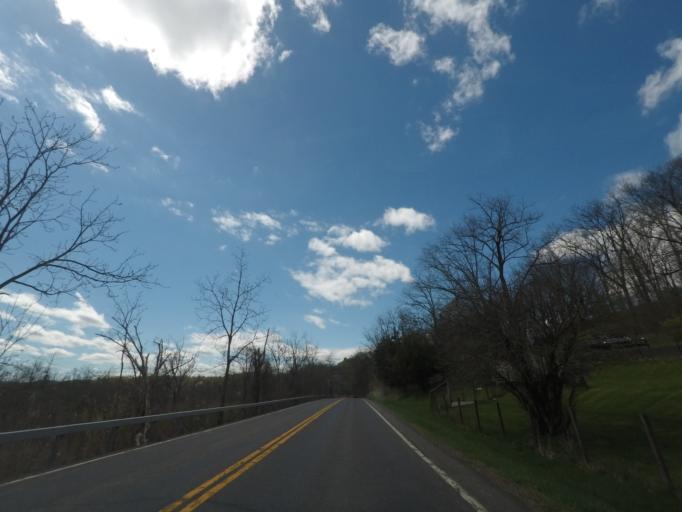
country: US
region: New York
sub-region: Greene County
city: Athens
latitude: 42.2573
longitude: -73.8177
